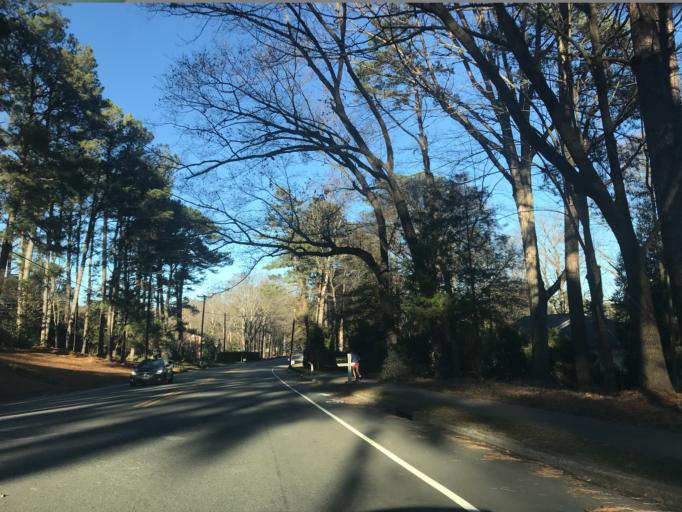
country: US
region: North Carolina
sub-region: Wake County
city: West Raleigh
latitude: 35.8271
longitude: -78.6766
